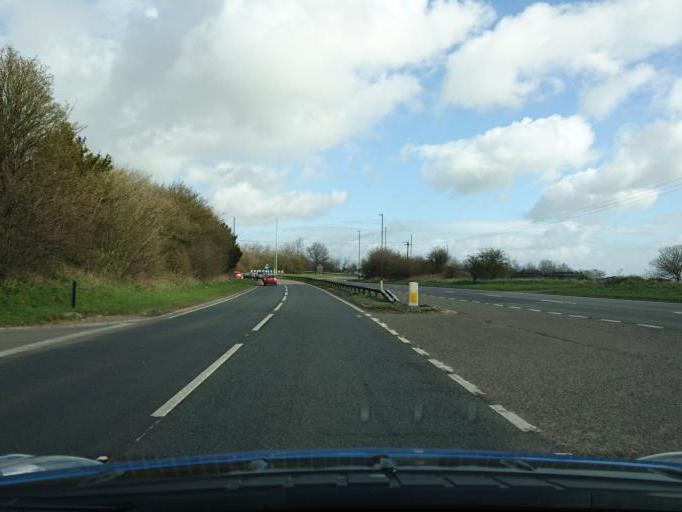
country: GB
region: England
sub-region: South Gloucestershire
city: Hinton
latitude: 51.4997
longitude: -2.3506
